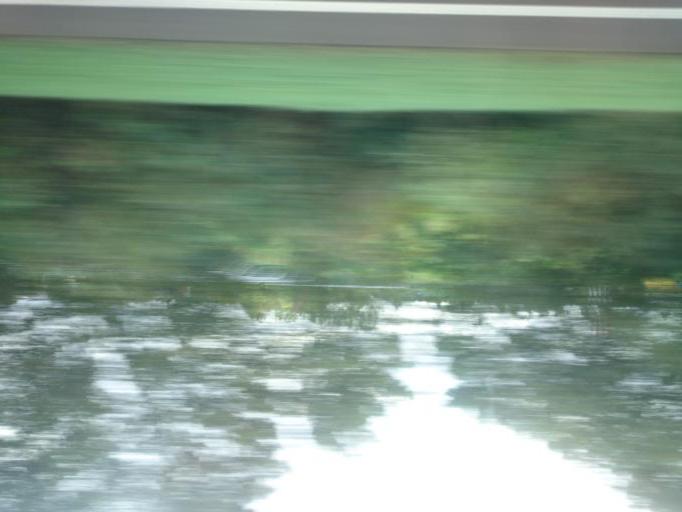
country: DE
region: Saxony-Anhalt
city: Hohenthurm
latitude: 51.5270
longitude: 12.1055
